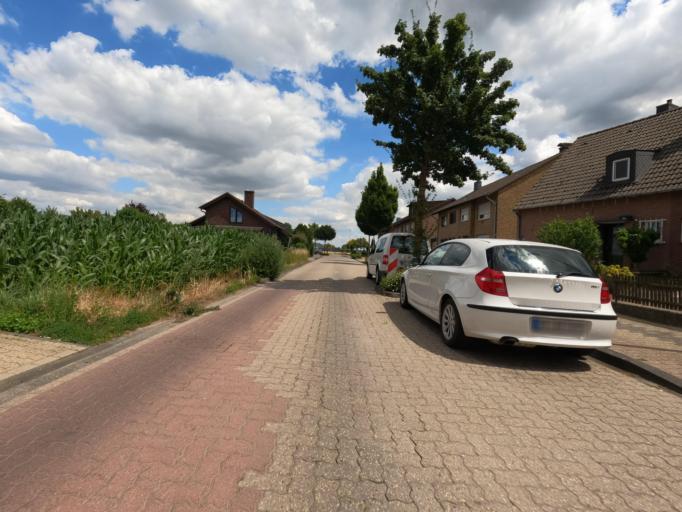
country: DE
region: North Rhine-Westphalia
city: Geilenkirchen
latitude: 50.9851
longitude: 6.0809
